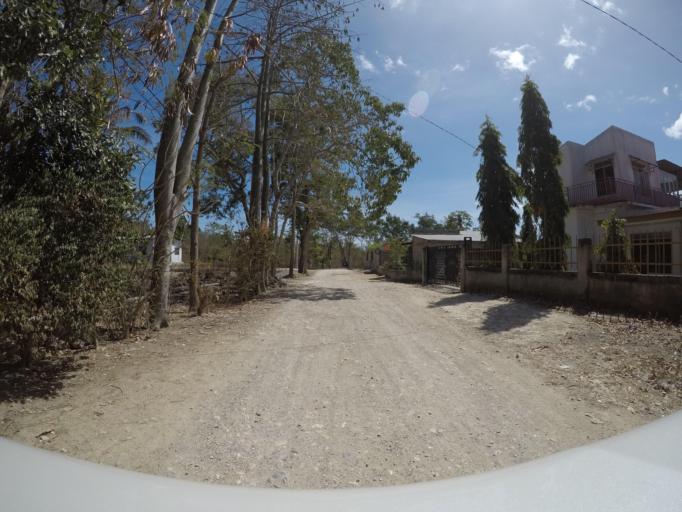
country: TL
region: Baucau
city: Baucau
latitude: -8.4709
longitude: 126.4546
